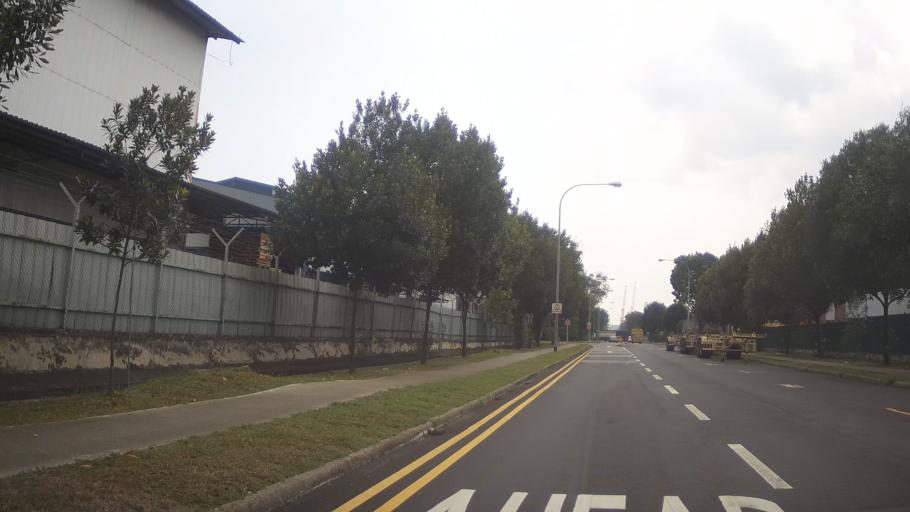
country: MY
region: Johor
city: Johor Bahru
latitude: 1.3122
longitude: 103.6623
